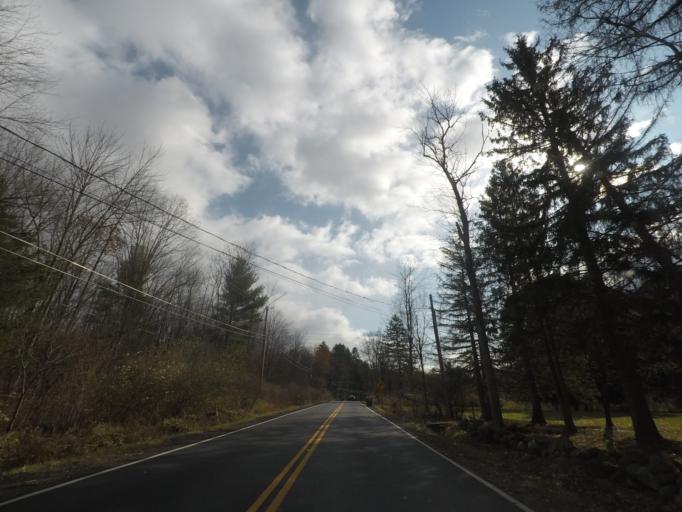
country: US
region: New York
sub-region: Saratoga County
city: Country Knolls
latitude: 42.9422
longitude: -73.8525
